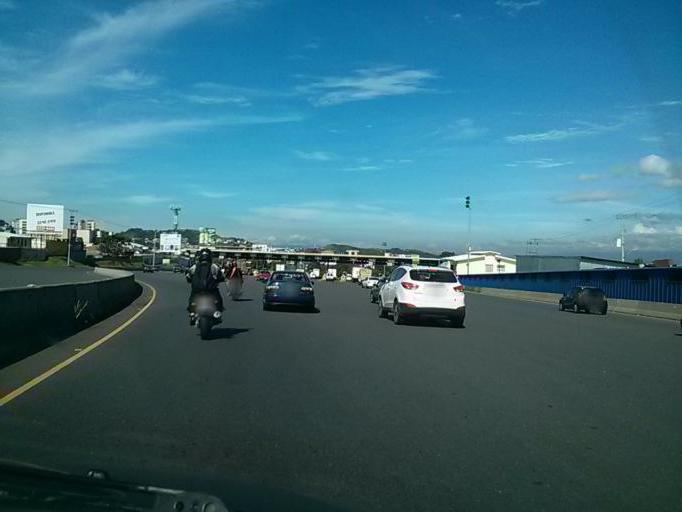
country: CR
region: San Jose
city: San Rafael
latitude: 9.9375
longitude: -84.1340
